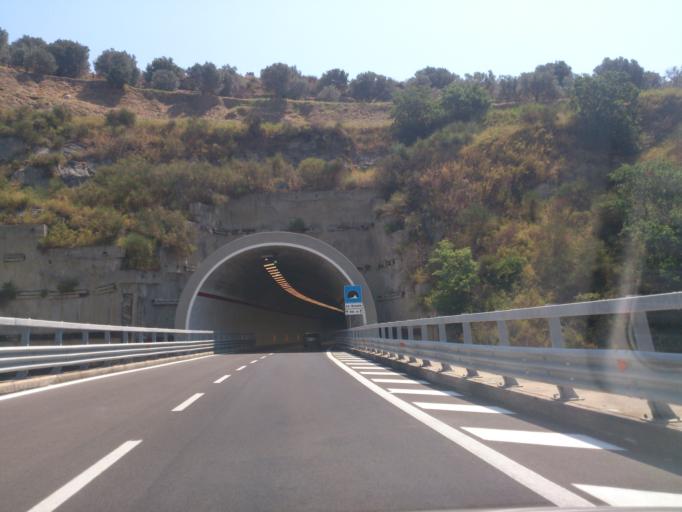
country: IT
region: Calabria
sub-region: Provincia di Reggio Calabria
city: Roccella Ionica
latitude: 38.3299
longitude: 16.4090
